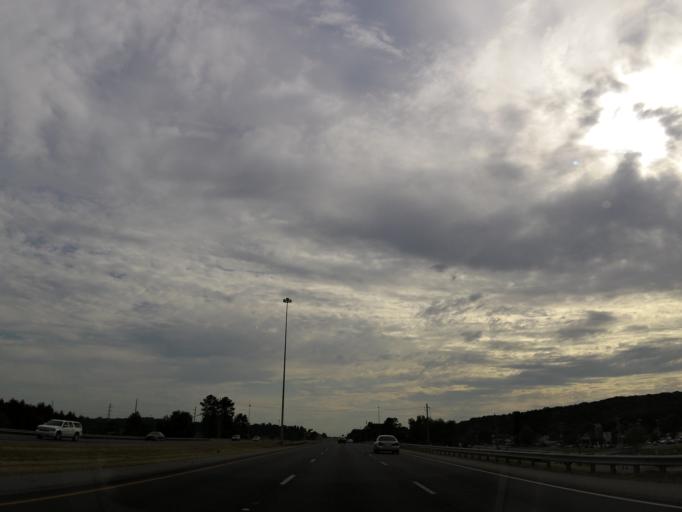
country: US
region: Alabama
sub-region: Madison County
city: Madison
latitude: 34.6908
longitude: -86.7144
